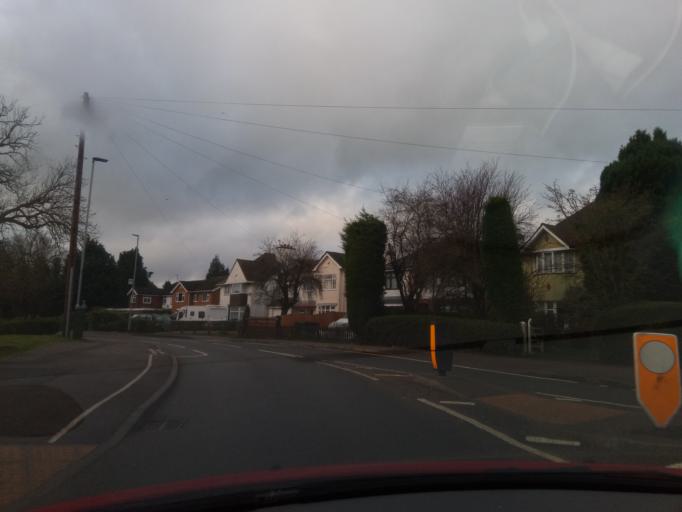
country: GB
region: England
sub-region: Leicestershire
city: Sileby
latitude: 52.7400
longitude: -1.1017
